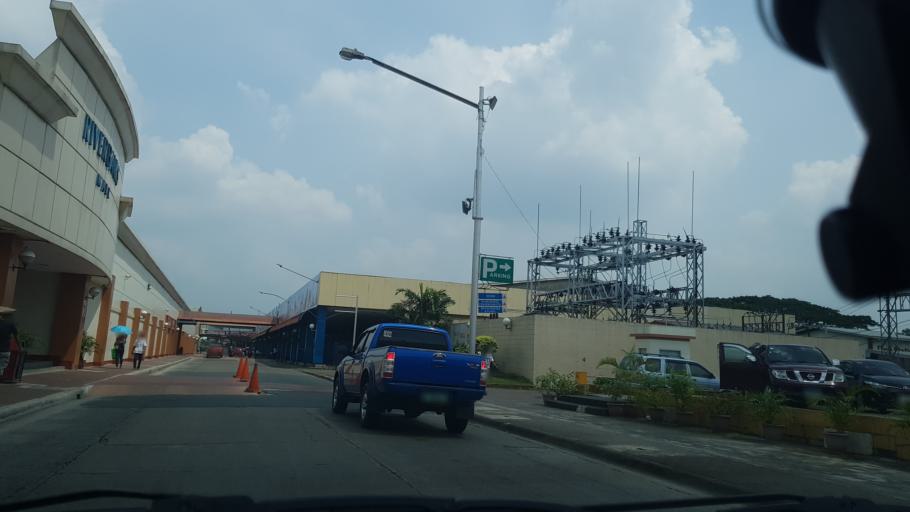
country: PH
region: Metro Manila
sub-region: Marikina
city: Calumpang
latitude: 14.6304
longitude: 121.0826
